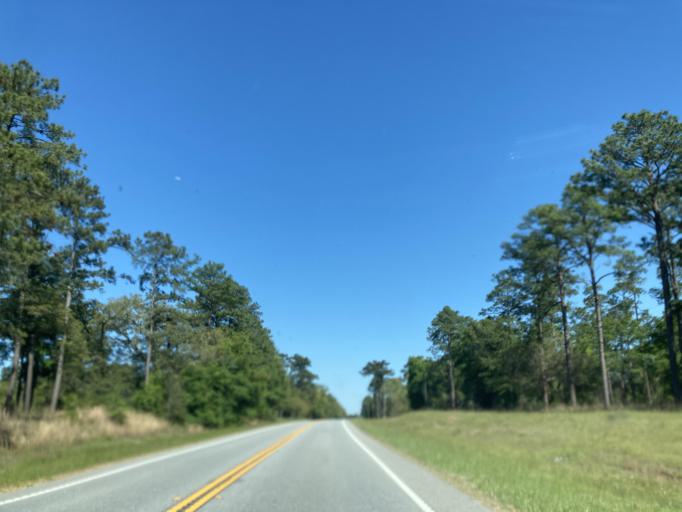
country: US
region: Georgia
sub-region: Baker County
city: Newton
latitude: 31.2135
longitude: -84.4705
